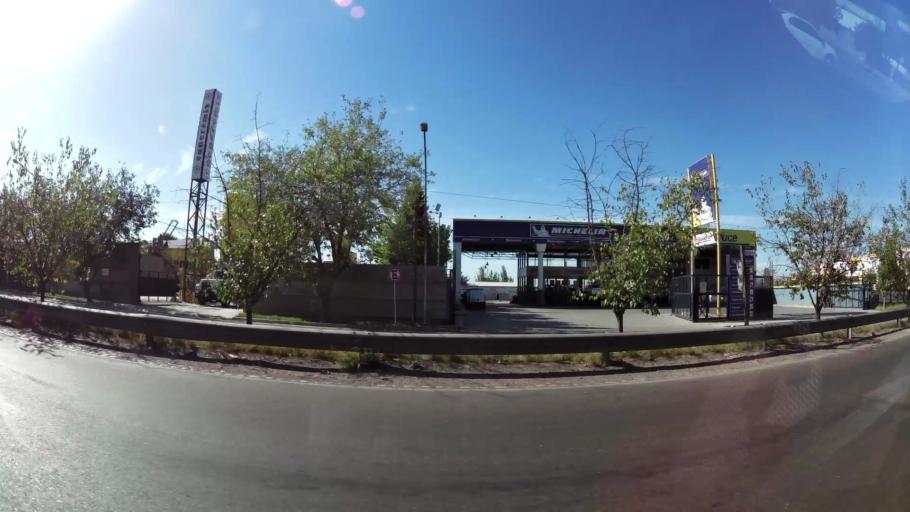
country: AR
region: Mendoza
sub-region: Departamento de Godoy Cruz
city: Godoy Cruz
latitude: -32.9254
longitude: -68.8284
